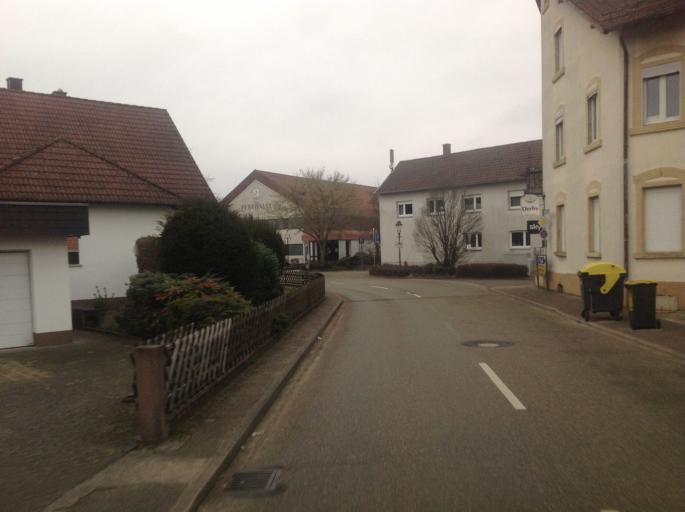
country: DE
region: Baden-Wuerttemberg
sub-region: Karlsruhe Region
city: Iffezheim
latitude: 48.8205
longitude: 8.1422
